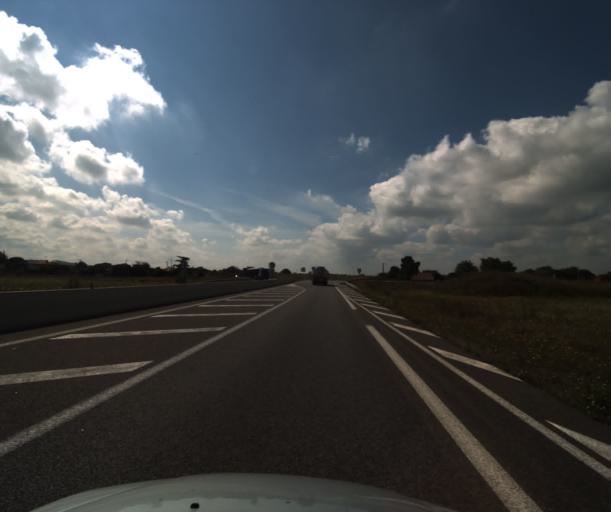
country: FR
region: Midi-Pyrenees
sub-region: Departement de la Haute-Garonne
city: Vernet
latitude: 43.4298
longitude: 1.4182
